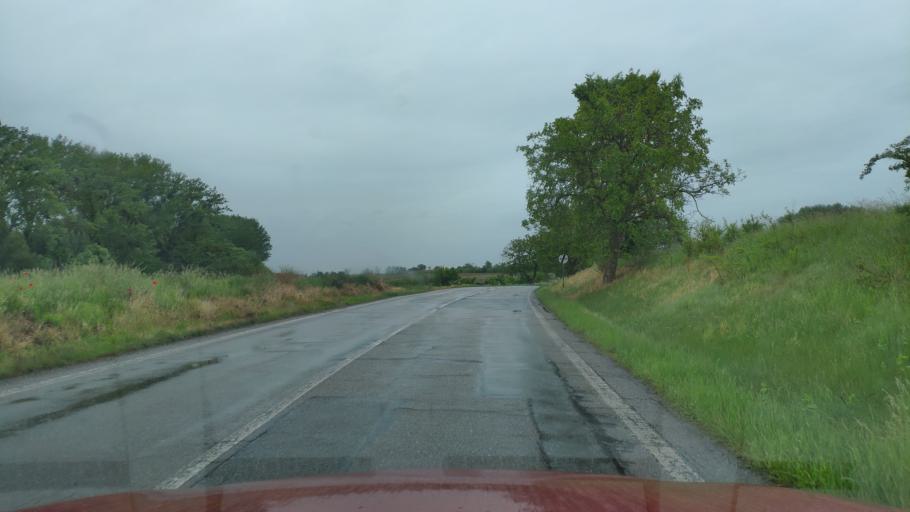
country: HU
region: Borsod-Abauj-Zemplen
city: Ricse
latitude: 48.4349
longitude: 21.9571
